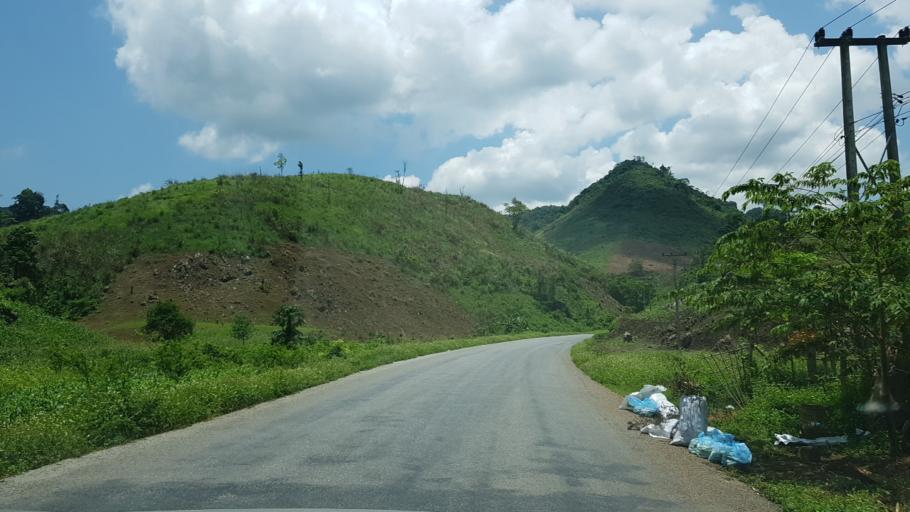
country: LA
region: Vientiane
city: Muang Kasi
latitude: 19.1354
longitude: 102.2873
